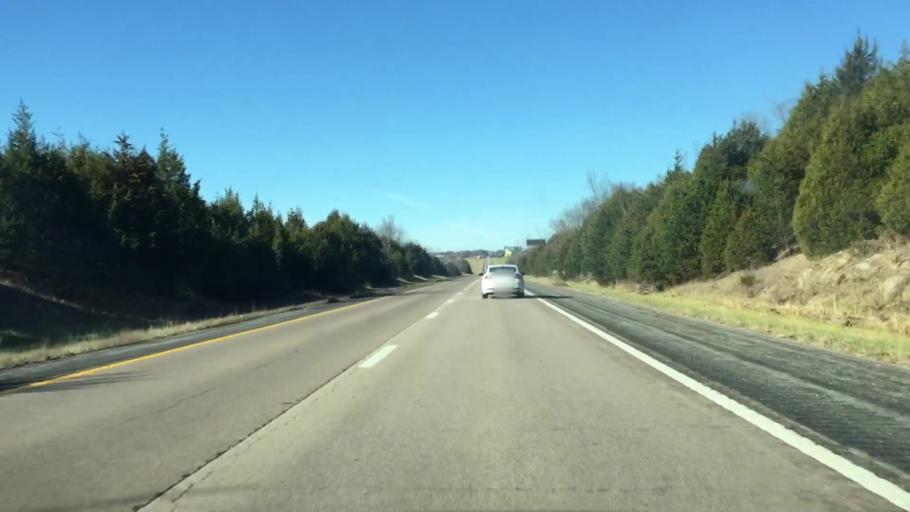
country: US
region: Missouri
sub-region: Miller County
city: Eldon
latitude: 38.3677
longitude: -92.4886
